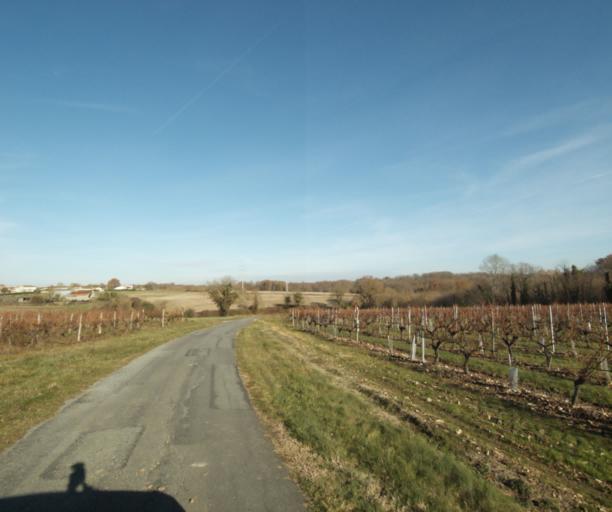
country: FR
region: Poitou-Charentes
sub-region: Departement de la Charente-Maritime
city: Ecoyeux
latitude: 45.7721
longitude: -0.5043
